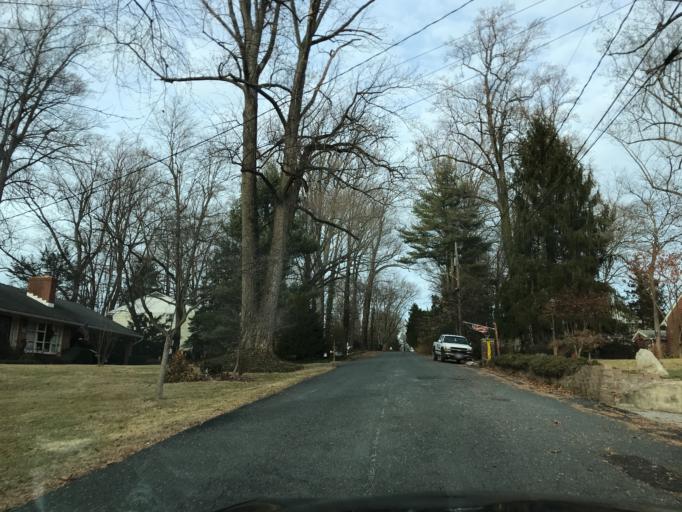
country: US
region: Maryland
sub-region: Baltimore County
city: Kingsville
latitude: 39.4483
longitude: -76.4102
